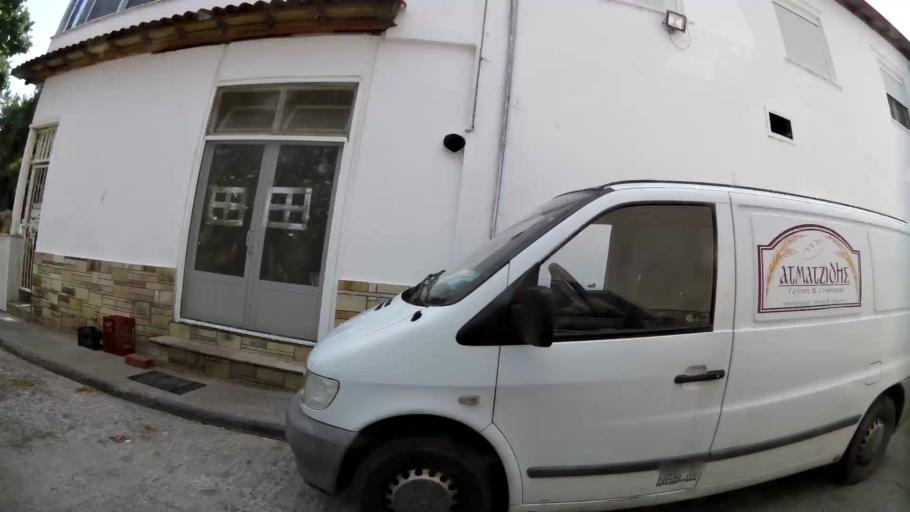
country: GR
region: Central Macedonia
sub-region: Nomos Pierias
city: Makrygialos
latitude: 40.4152
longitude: 22.6036
